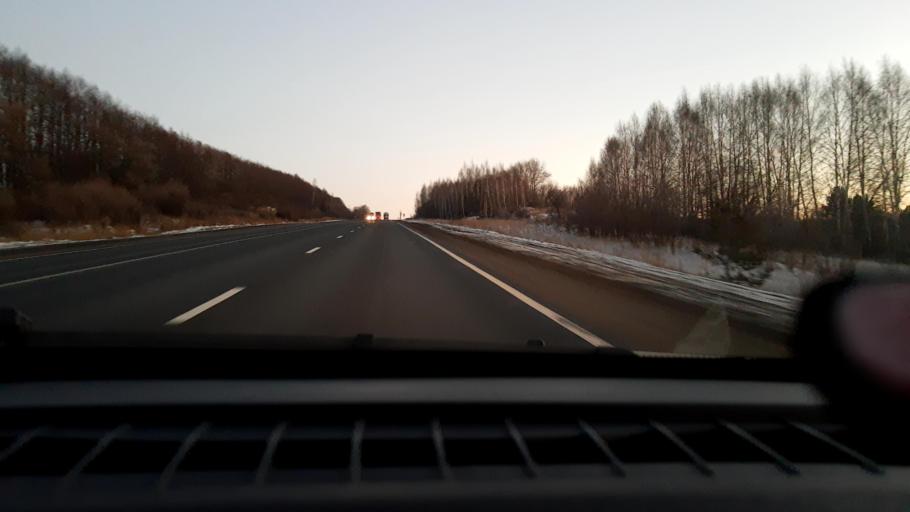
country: RU
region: Nizjnij Novgorod
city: Pervoye Maya
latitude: 55.9982
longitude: 44.7503
